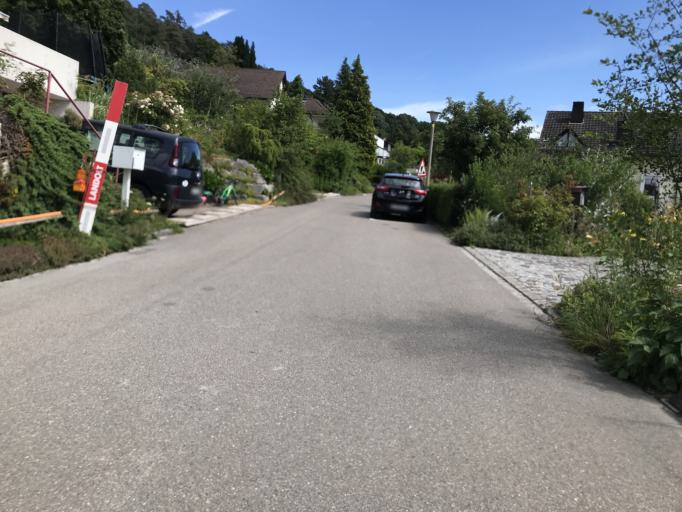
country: CH
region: Zurich
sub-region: Bezirk Winterthur
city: Neftenbach / Dorf Neftenbach
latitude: 47.5240
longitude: 8.6718
